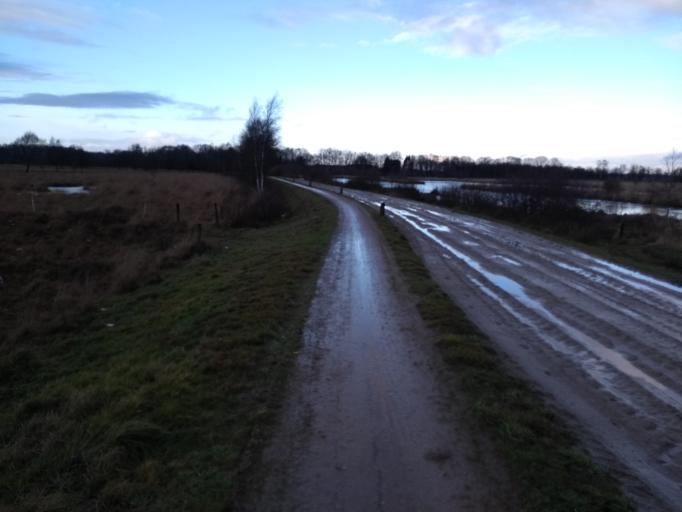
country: NL
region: Overijssel
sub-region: Gemeente Wierden
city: Wierden
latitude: 52.3772
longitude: 6.5164
